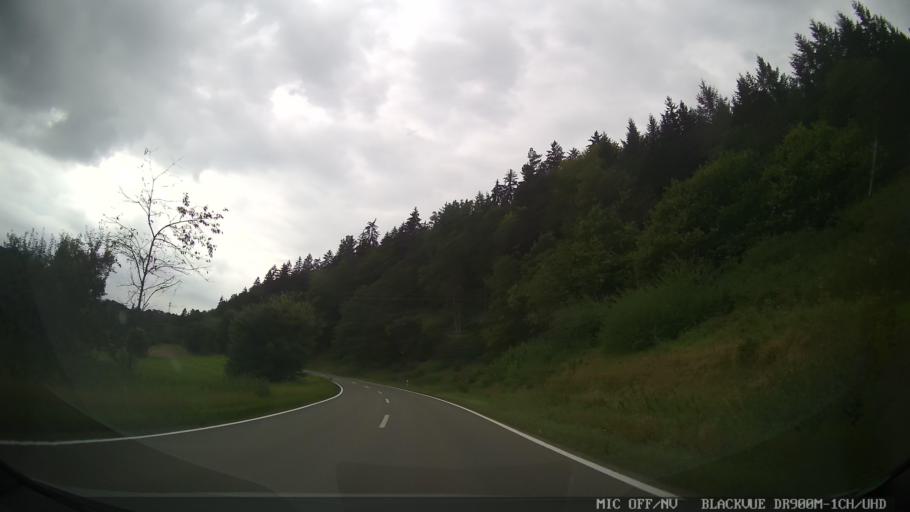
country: DE
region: Baden-Wuerttemberg
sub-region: Freiburg Region
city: Fridingen an der Donau
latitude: 48.0177
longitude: 8.9169
